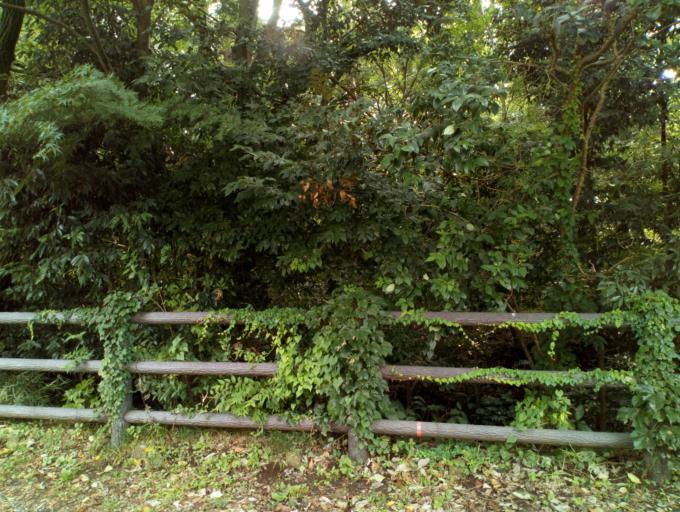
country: JP
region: Tokyo
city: Musashino
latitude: 35.6967
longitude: 139.5729
